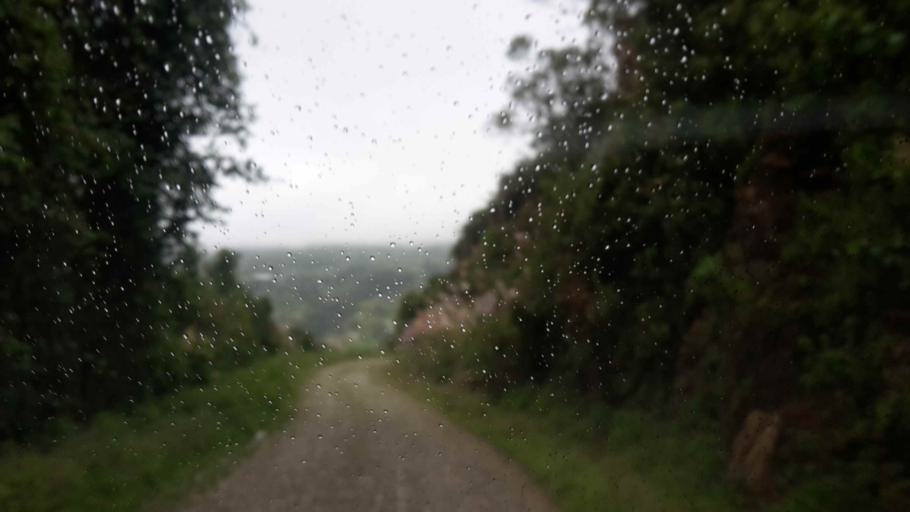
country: BO
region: Cochabamba
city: Colomi
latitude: -17.1336
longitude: -65.9441
